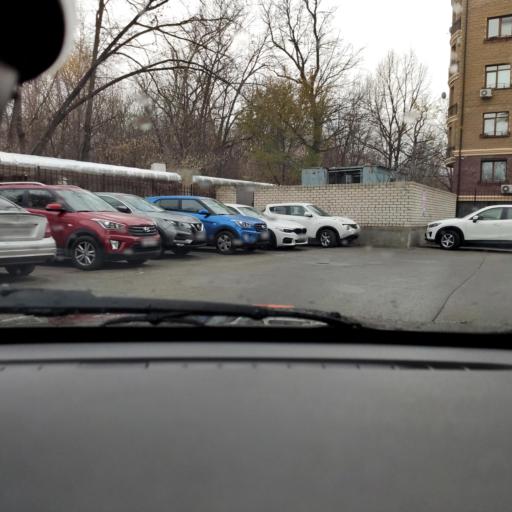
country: RU
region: Samara
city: Tol'yatti
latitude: 53.5365
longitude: 49.3624
